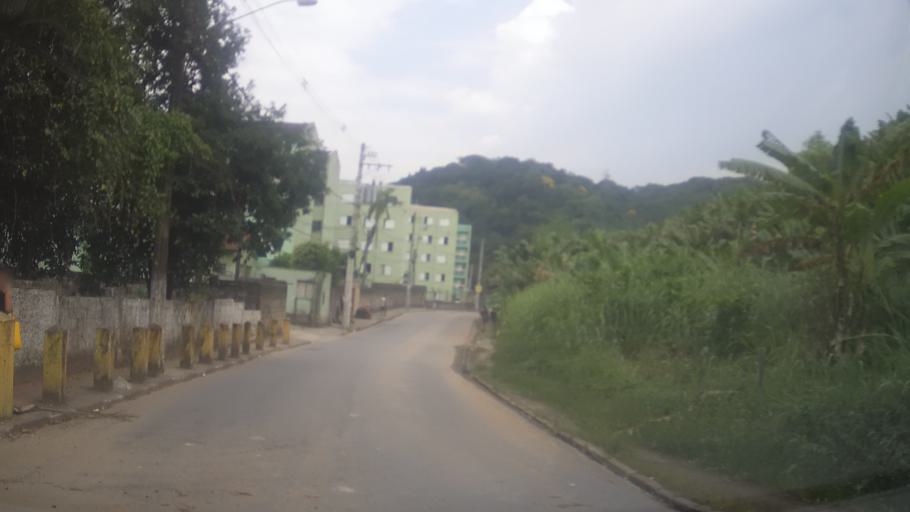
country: BR
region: Sao Paulo
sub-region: Santos
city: Santos
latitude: -23.9418
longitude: -46.3509
